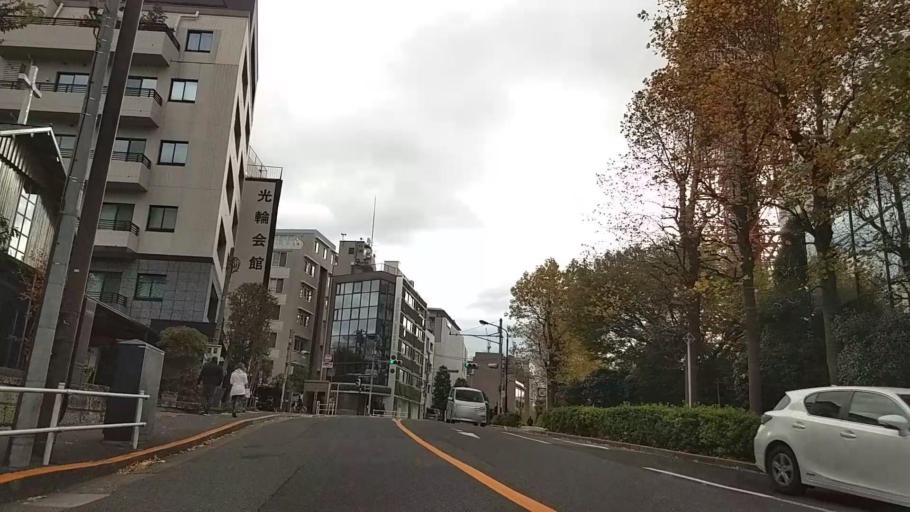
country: JP
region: Tokyo
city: Tokyo
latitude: 35.6597
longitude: 139.7436
